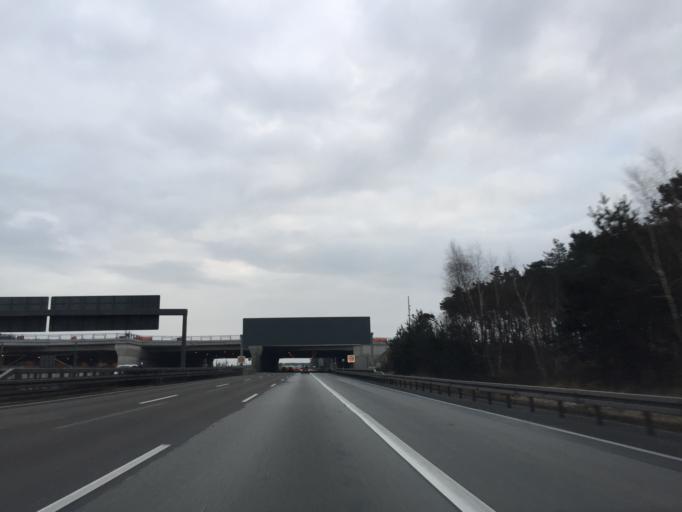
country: DE
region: Hesse
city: Kelsterbach
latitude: 50.0345
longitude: 8.5138
